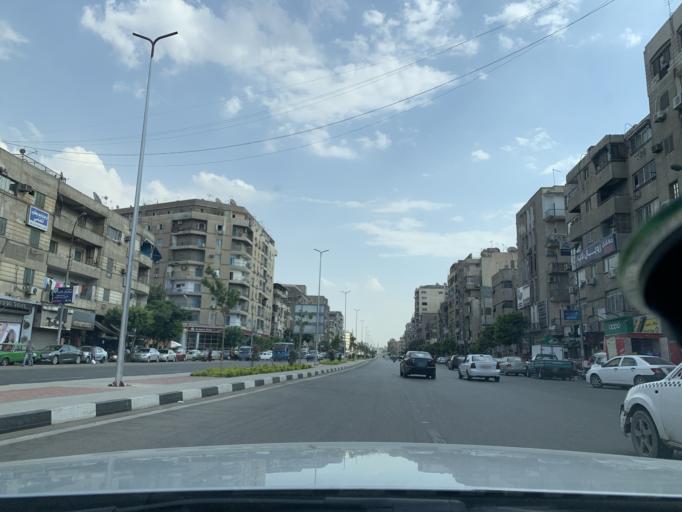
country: EG
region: Muhafazat al Qahirah
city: Cairo
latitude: 30.1049
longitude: 31.3437
